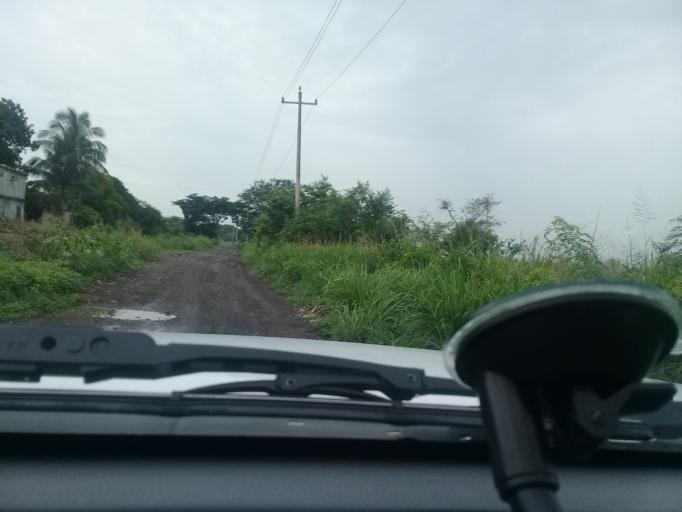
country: MX
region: Veracruz
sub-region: Puente Nacional
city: Cabezas
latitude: 19.3619
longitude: -96.4081
